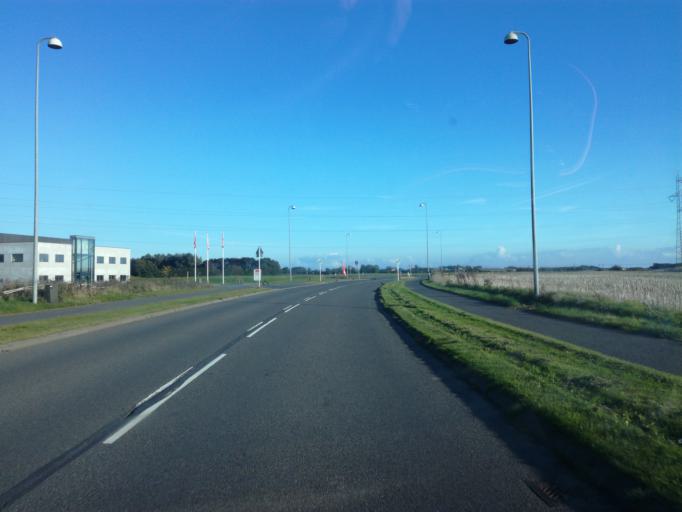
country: DK
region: South Denmark
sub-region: Fredericia Kommune
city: Taulov
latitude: 55.5549
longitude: 9.6598
